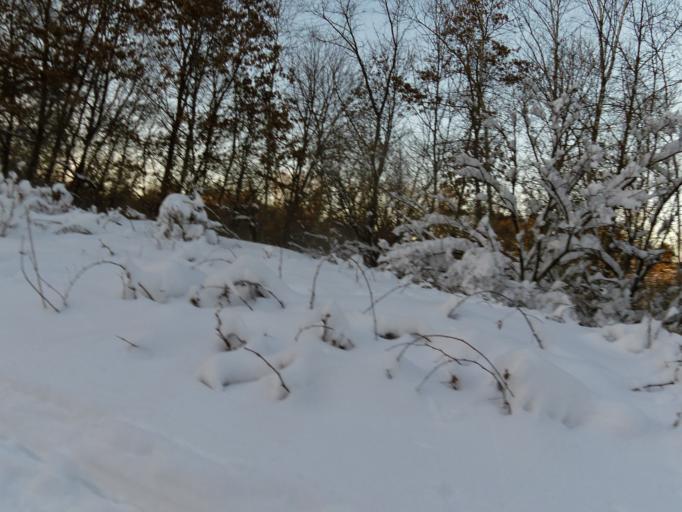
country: US
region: Minnesota
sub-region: Washington County
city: Lake Elmo
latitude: 44.9697
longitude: -92.9051
